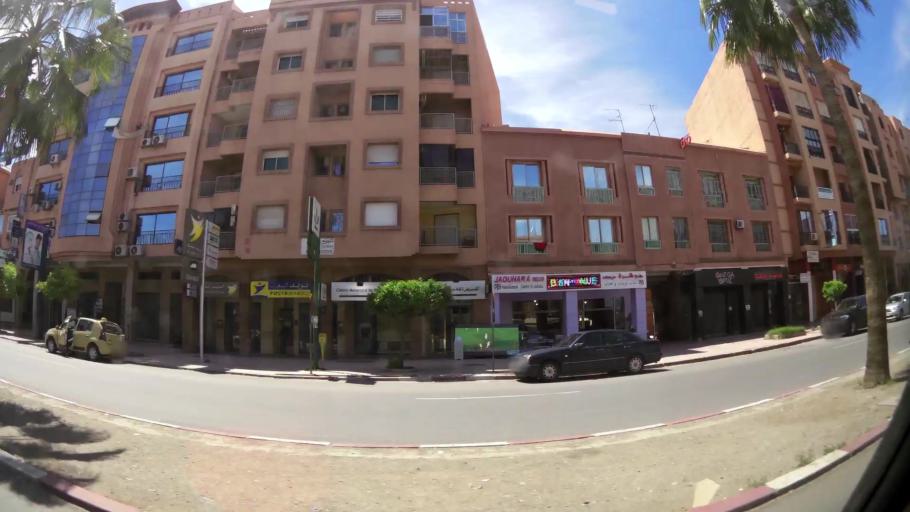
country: MA
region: Marrakech-Tensift-Al Haouz
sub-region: Marrakech
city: Marrakesh
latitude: 31.6484
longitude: -8.0010
